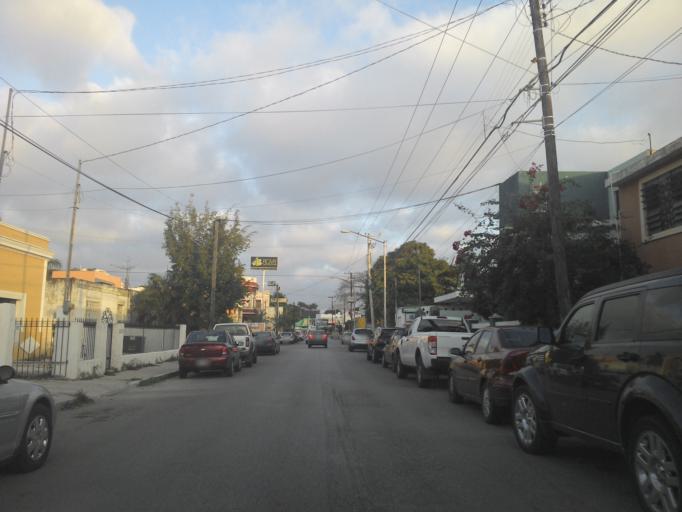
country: MX
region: Yucatan
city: Merida
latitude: 20.9926
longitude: -89.6155
